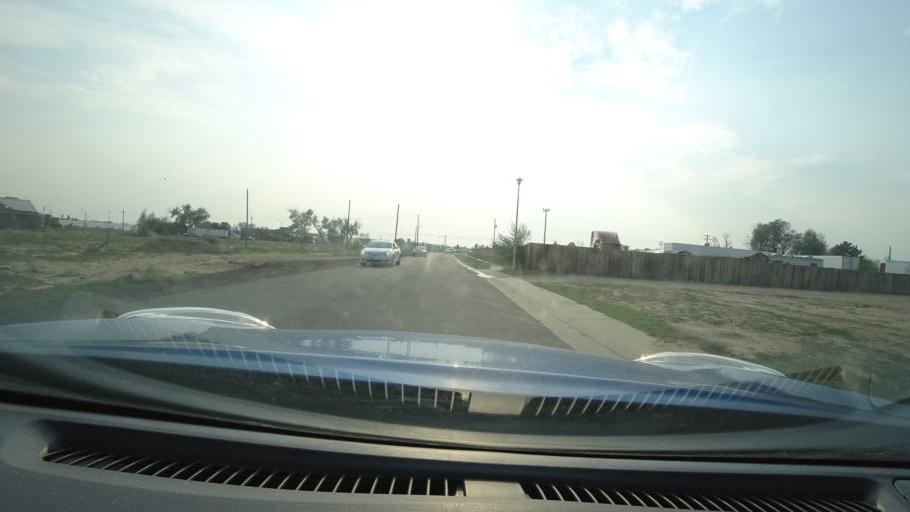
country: US
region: Colorado
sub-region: Adams County
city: Aurora
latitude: 39.7474
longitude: -104.7707
